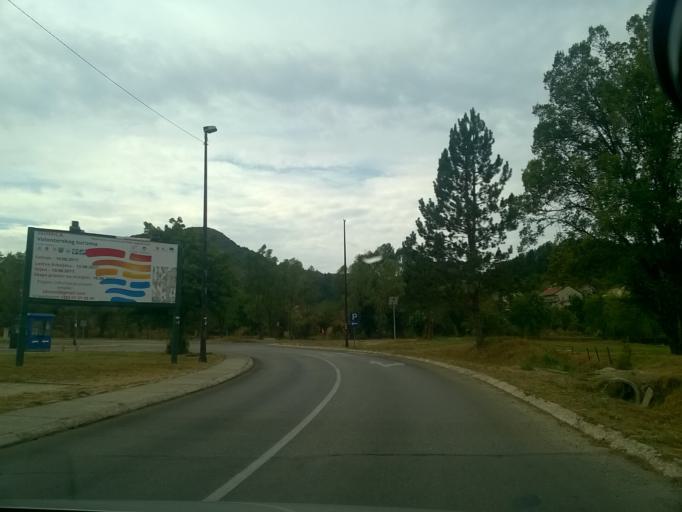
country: ME
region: Cetinje
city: Cetinje
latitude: 42.3855
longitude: 18.9229
